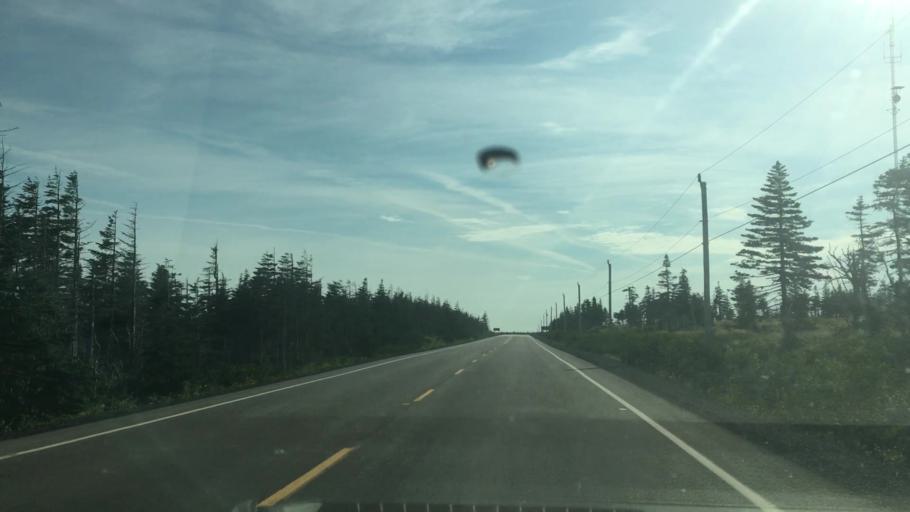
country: CA
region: Nova Scotia
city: Sydney Mines
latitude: 46.8188
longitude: -60.6688
